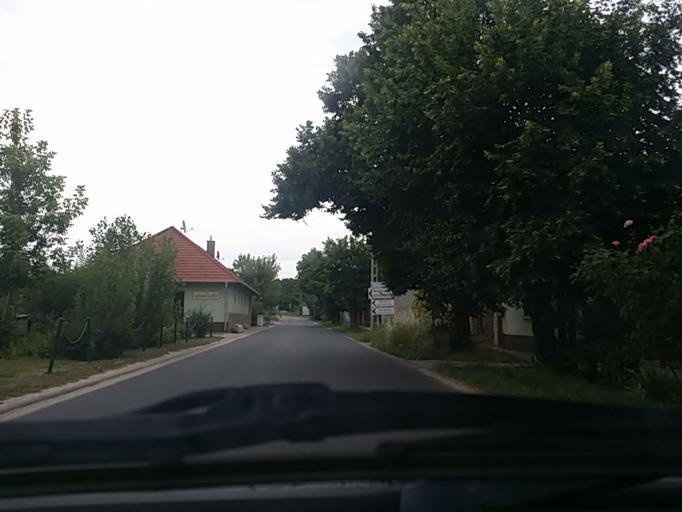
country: HU
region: Pest
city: Urom
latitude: 47.5978
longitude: 19.0166
